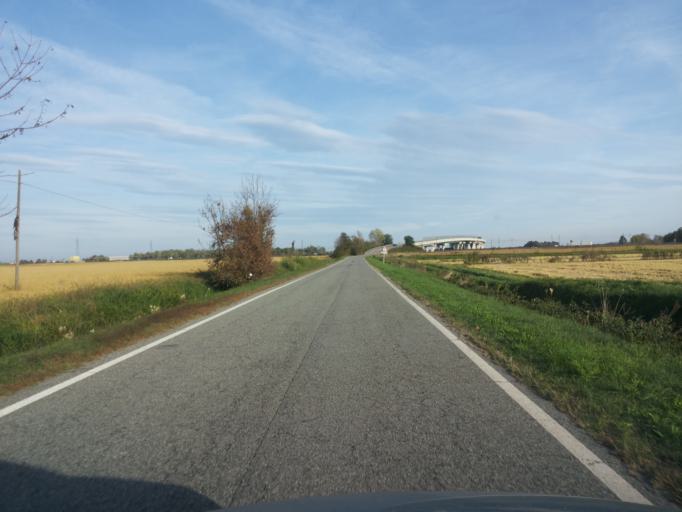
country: IT
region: Piedmont
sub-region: Provincia di Vercelli
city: Carisio
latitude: 45.4295
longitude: 8.1916
